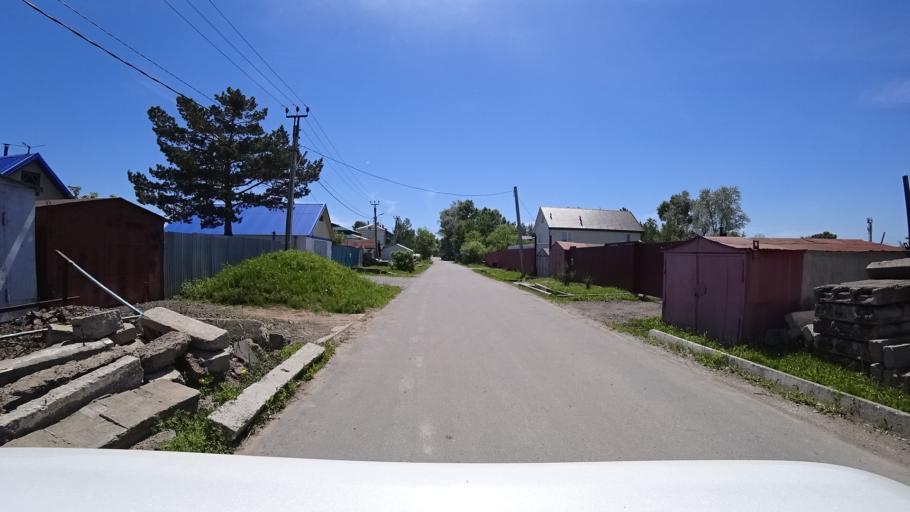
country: RU
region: Khabarovsk Krai
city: Topolevo
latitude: 48.5108
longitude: 135.1707
